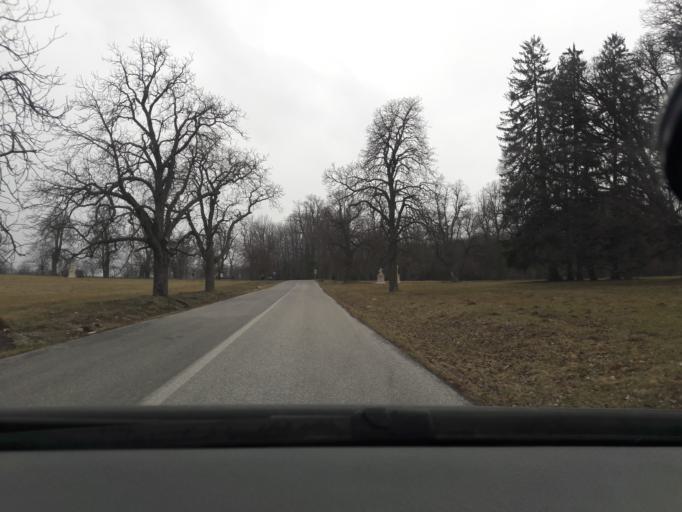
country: SK
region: Bratislavsky
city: Modra
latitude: 48.3949
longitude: 17.3374
